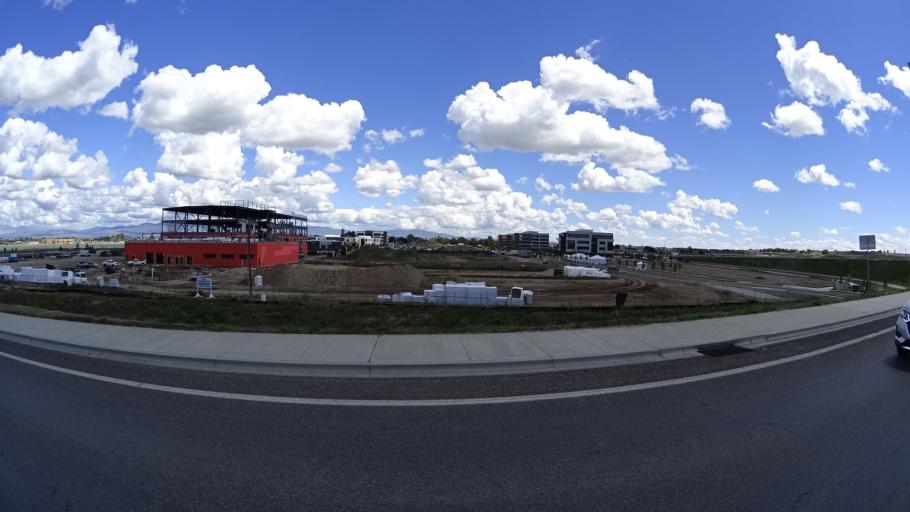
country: US
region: Idaho
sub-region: Ada County
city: Meridian
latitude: 43.5959
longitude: -116.4341
